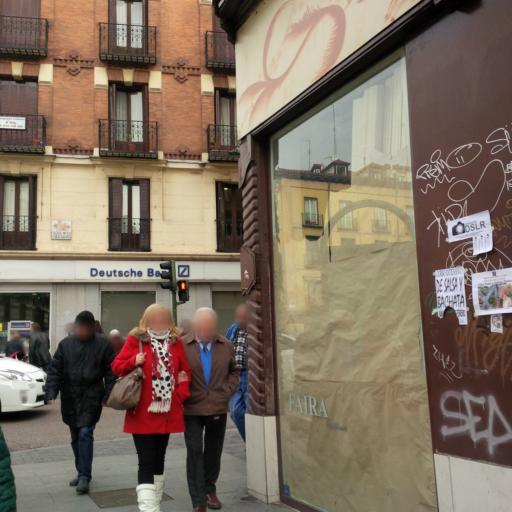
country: ES
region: Madrid
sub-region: Provincia de Madrid
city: Madrid
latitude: 40.4132
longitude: -3.7074
